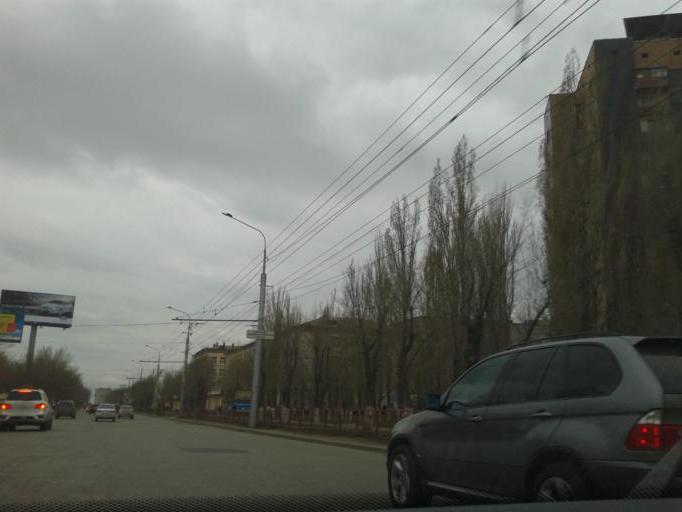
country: RU
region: Volgograd
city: Volgograd
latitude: 48.7380
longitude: 44.4928
